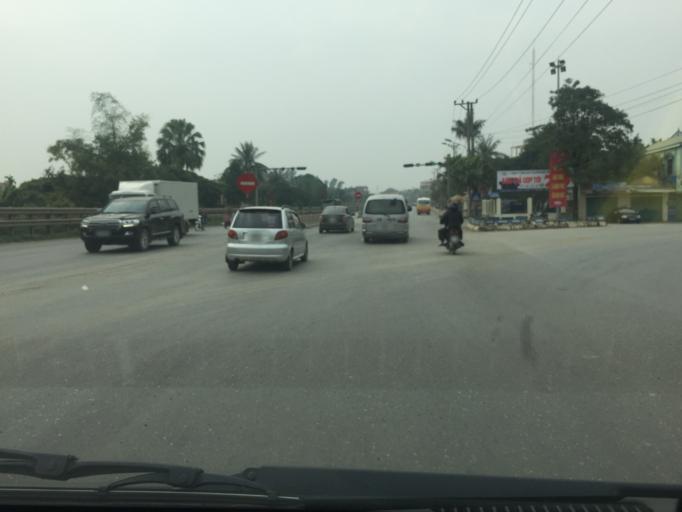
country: VN
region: Ninh Binh
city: Thi Tran Tam Diep
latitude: 20.1621
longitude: 105.9296
